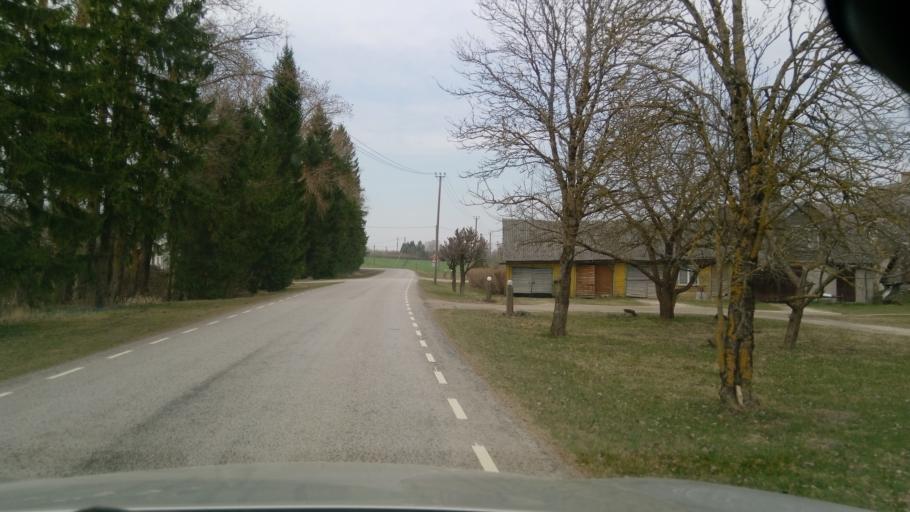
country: EE
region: Jaervamaa
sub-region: Tueri vald
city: Sarevere
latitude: 58.7821
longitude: 25.4797
